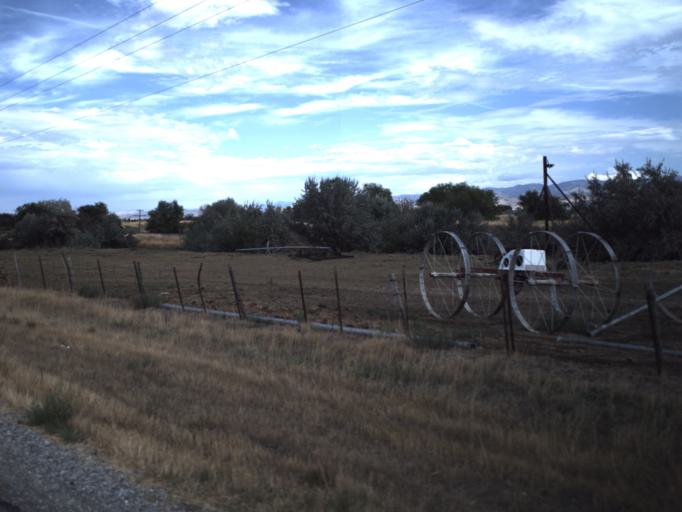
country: US
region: Utah
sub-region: Cache County
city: Lewiston
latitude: 41.9887
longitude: -111.9547
